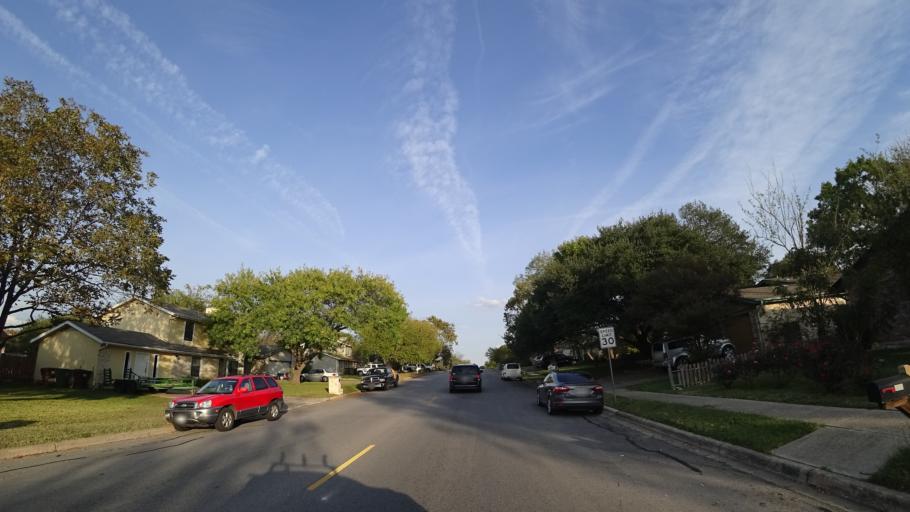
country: US
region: Texas
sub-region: Williamson County
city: Round Rock
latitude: 30.5023
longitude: -97.6691
